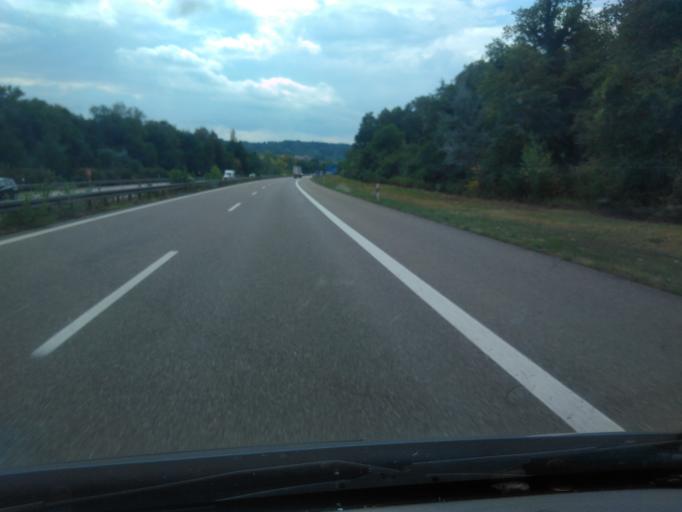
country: DE
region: Baden-Wuerttemberg
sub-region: Freiburg Region
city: Bad Bellingen
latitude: 47.7465
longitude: 7.5503
